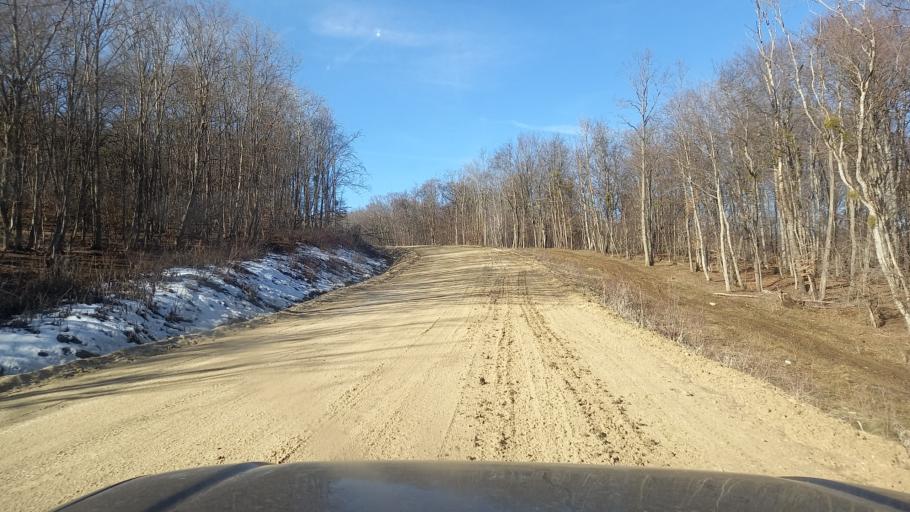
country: RU
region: Adygeya
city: Kamennomostskiy
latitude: 44.2805
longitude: 40.3252
